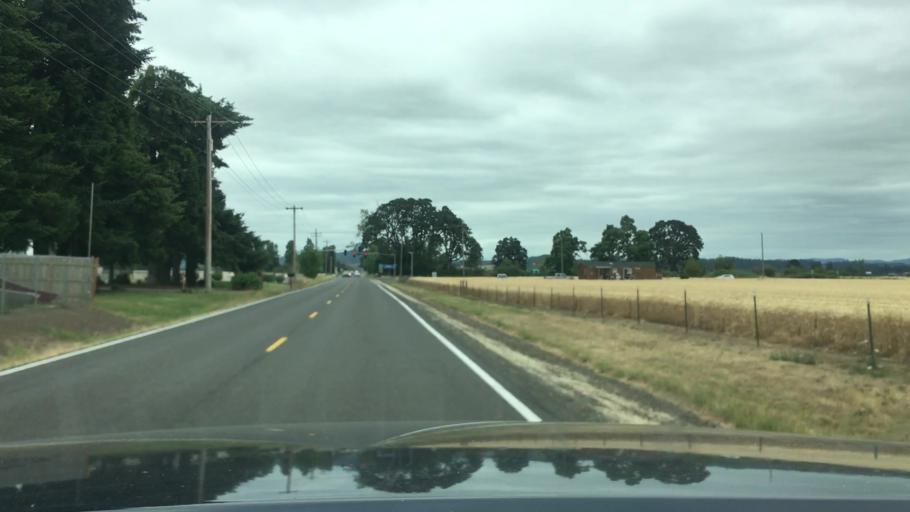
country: US
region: Oregon
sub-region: Lane County
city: Junction City
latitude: 44.1048
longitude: -123.2084
